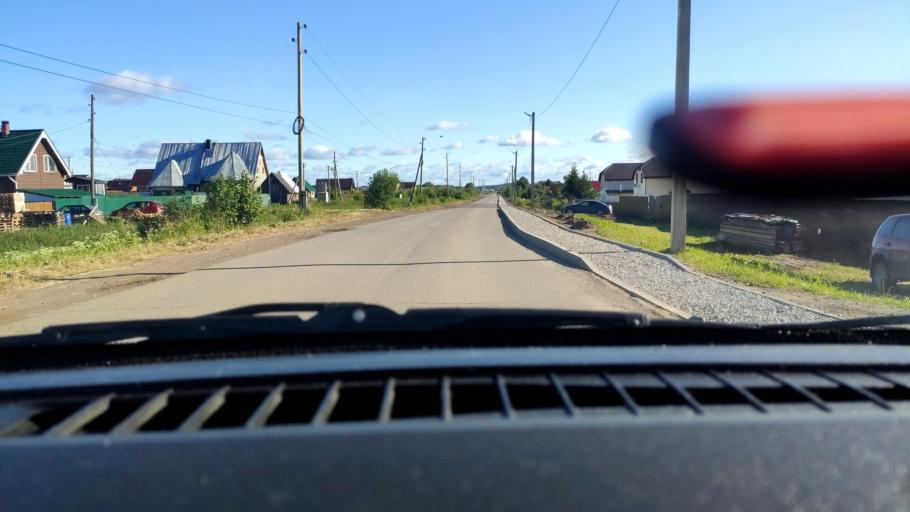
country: RU
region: Perm
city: Kultayevo
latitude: 57.8671
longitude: 55.9161
